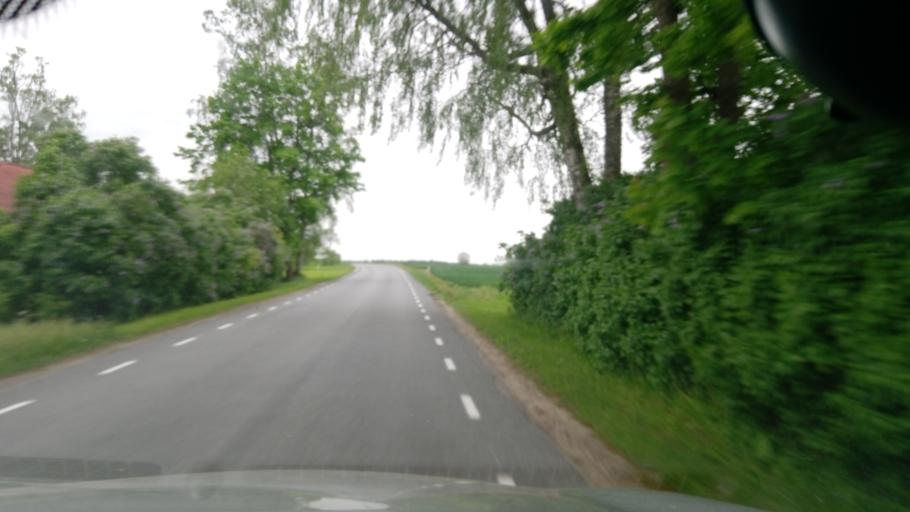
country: EE
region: Jaervamaa
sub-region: Koeru vald
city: Koeru
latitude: 59.0021
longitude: 26.0776
